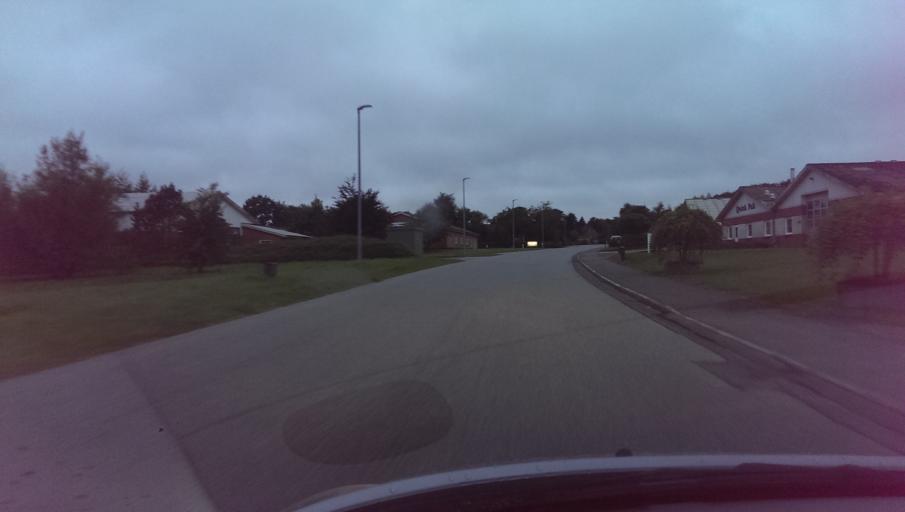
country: DK
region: South Denmark
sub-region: Varde Kommune
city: Olgod
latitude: 55.8143
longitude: 8.6299
